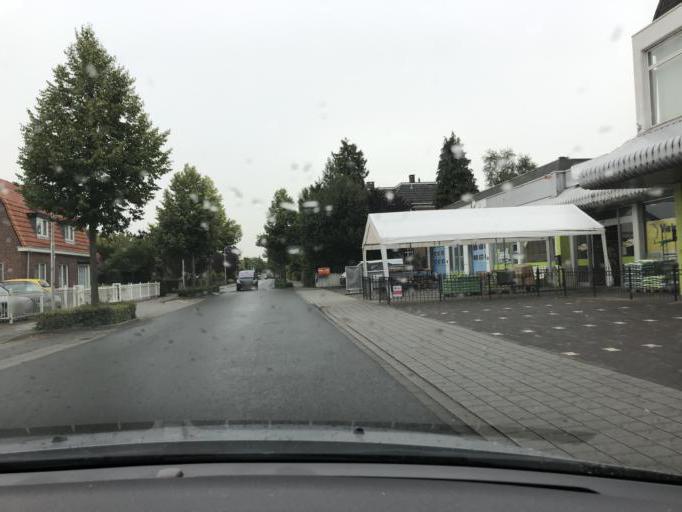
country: NL
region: Gelderland
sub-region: Berkelland
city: Eibergen
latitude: 52.0385
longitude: 6.6212
